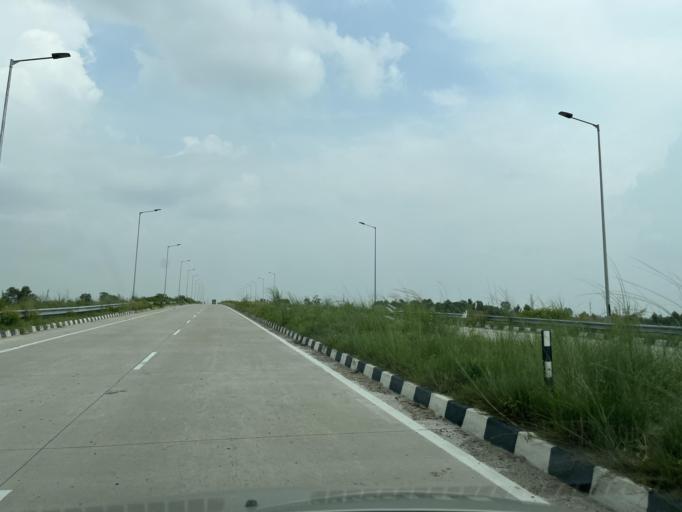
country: IN
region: Uttarakhand
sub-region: Udham Singh Nagar
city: Kashipur
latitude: 29.1757
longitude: 78.9423
